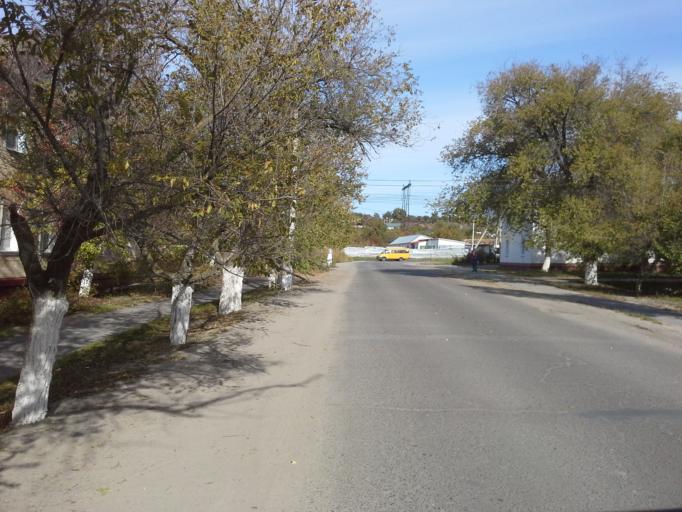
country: RU
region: Volgograd
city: Vodstroy
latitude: 48.8424
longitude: 44.6410
